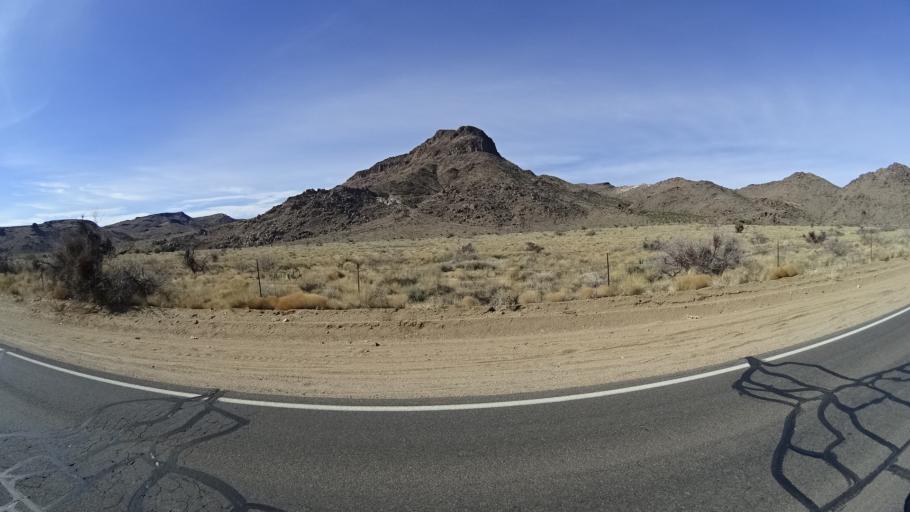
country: US
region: Arizona
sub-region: Mohave County
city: New Kingman-Butler
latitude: 35.2813
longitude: -114.0522
